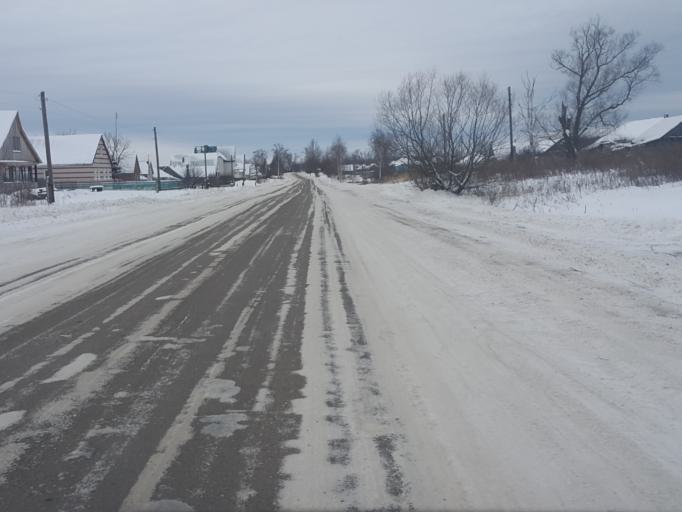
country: RU
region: Tambov
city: Platonovka
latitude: 52.8792
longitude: 41.8765
